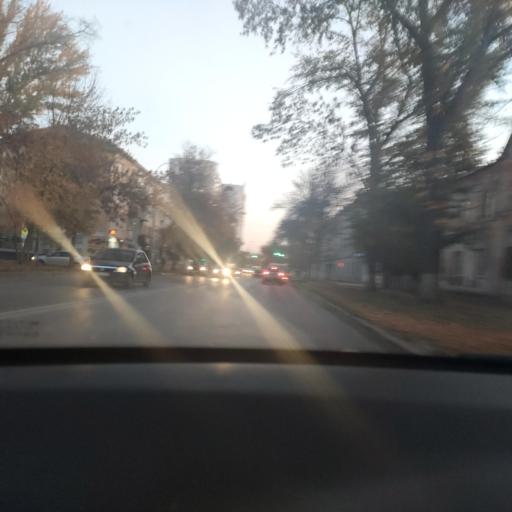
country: RU
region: Samara
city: Samara
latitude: 53.2018
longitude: 50.1783
